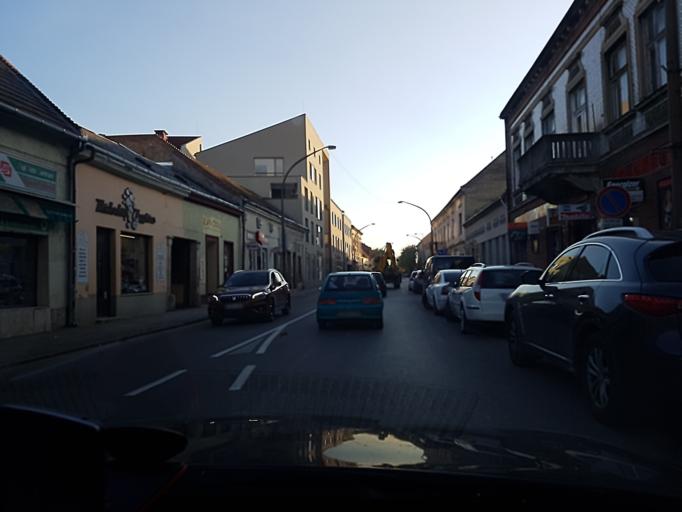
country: HU
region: Komarom-Esztergom
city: Esztergom
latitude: 47.7923
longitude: 18.7416
